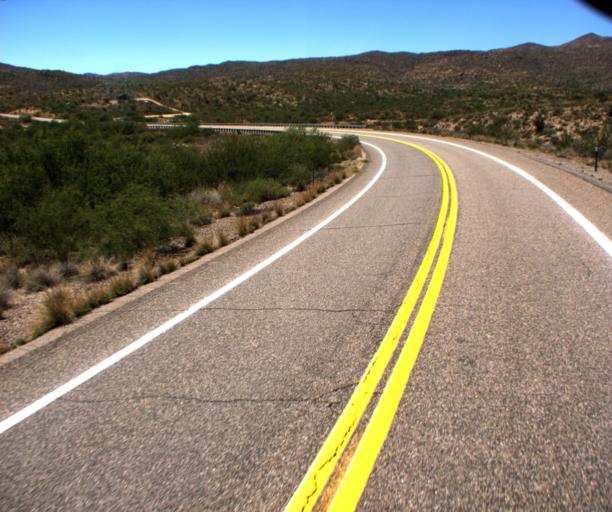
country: US
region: Arizona
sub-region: Yavapai County
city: Bagdad
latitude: 34.5167
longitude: -113.0760
